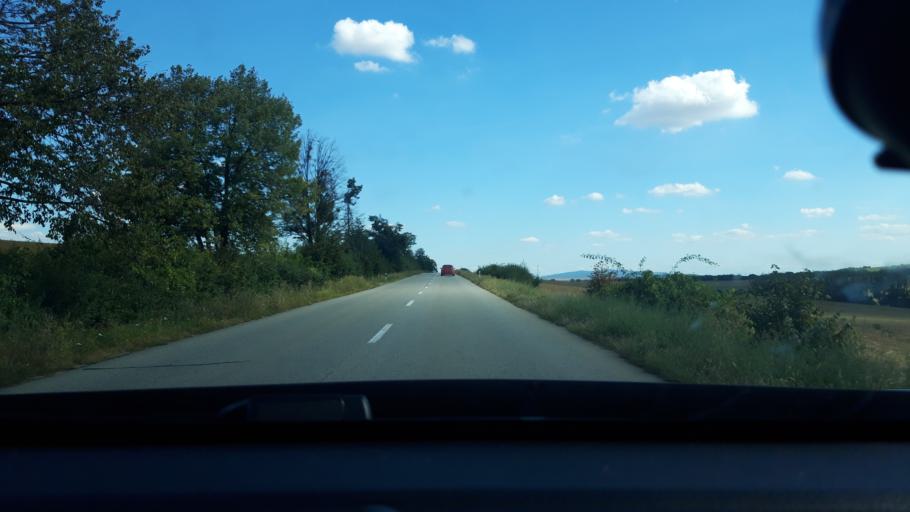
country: SK
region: Kosicky
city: Secovce
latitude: 48.6261
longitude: 21.5298
